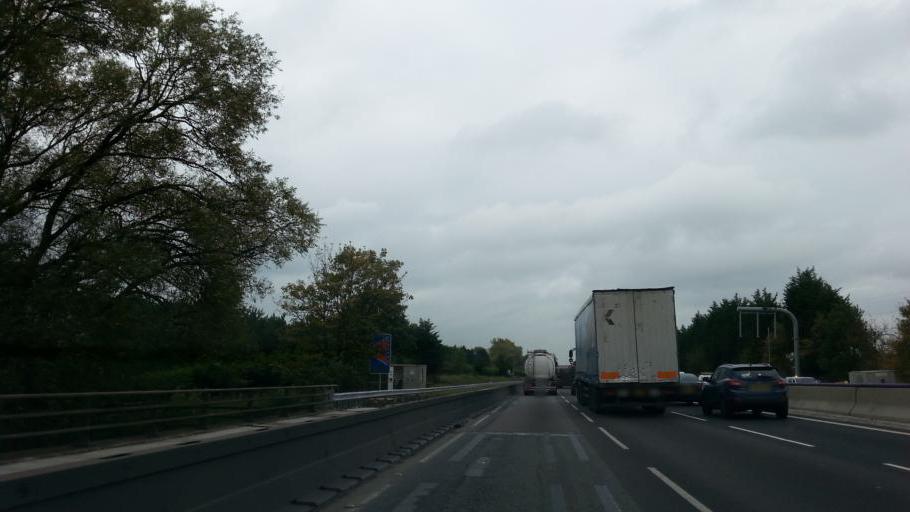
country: GB
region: England
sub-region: Cheshire East
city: Knutsford
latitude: 53.2657
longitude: -2.4014
